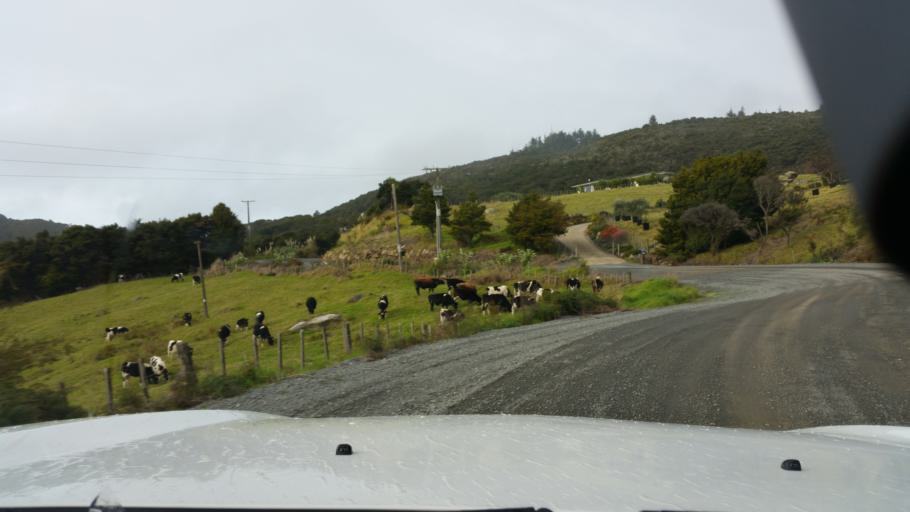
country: NZ
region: Northland
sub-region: Whangarei
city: Ngunguru
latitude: -35.7672
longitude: 174.5300
